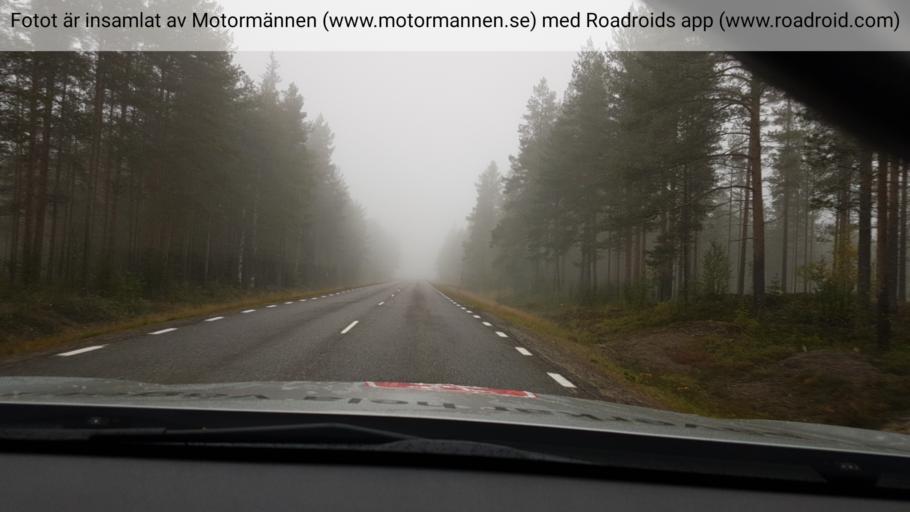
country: SE
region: Vaesterbotten
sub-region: Umea Kommun
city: Ersmark
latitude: 64.1076
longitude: 20.1728
